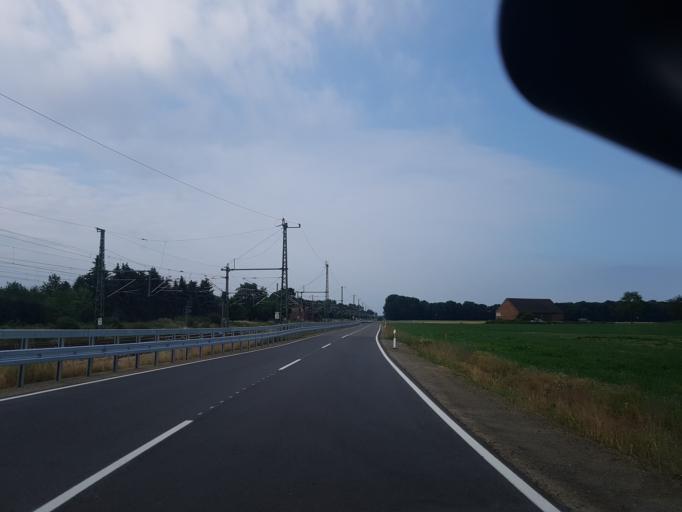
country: DE
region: Brandenburg
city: Schonewalde
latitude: 51.7036
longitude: 13.5965
